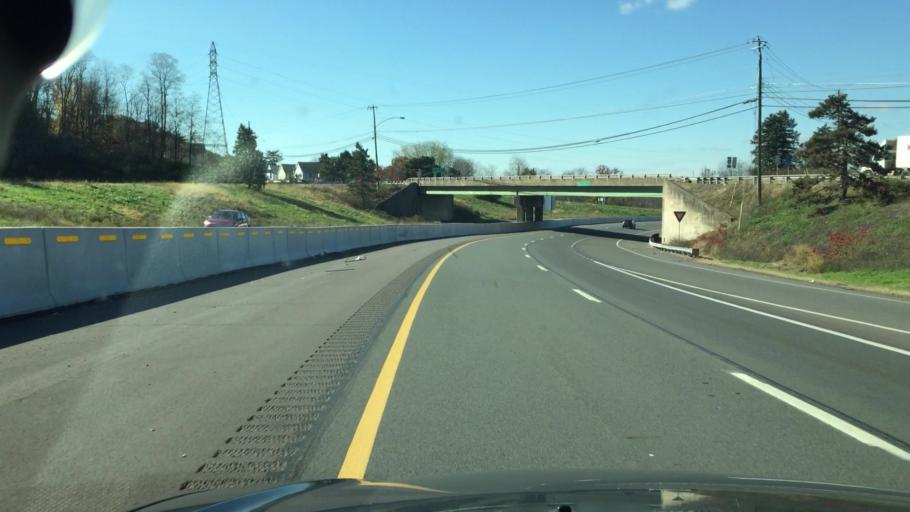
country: US
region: Pennsylvania
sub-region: Luzerne County
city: Ashley
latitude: 41.1996
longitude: -75.9190
